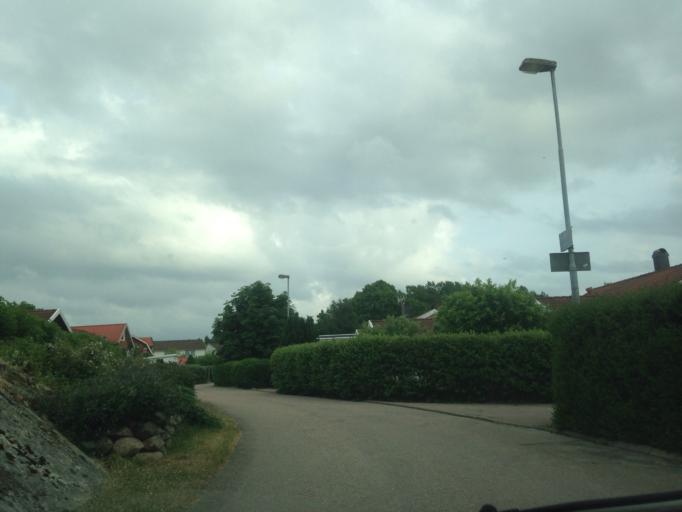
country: SE
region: Vaestra Goetaland
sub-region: Kungalvs Kommun
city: Kungalv
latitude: 57.8061
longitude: 11.9043
